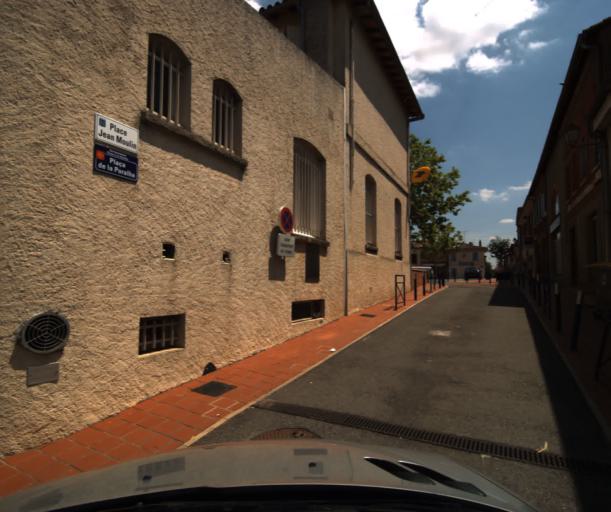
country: FR
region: Midi-Pyrenees
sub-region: Departement de la Haute-Garonne
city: Saint-Lys
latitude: 43.5133
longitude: 1.1748
